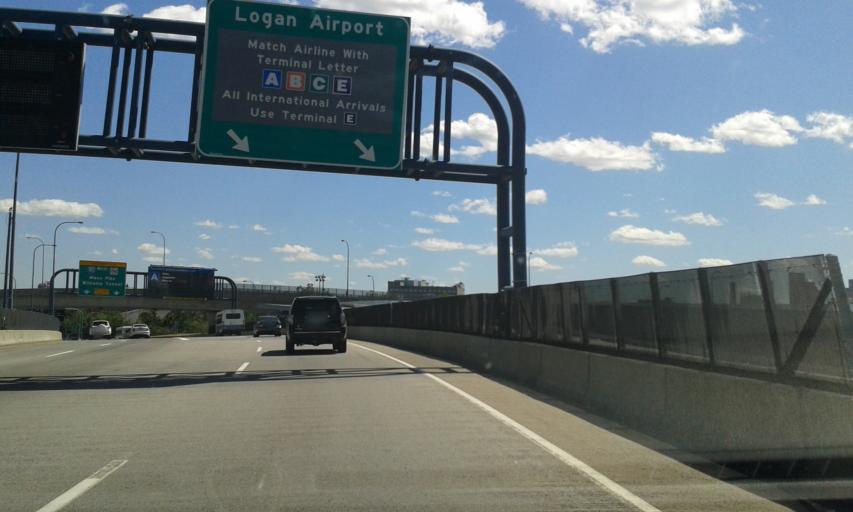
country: US
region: Massachusetts
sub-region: Suffolk County
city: Chelsea
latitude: 42.3753
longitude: -71.0297
